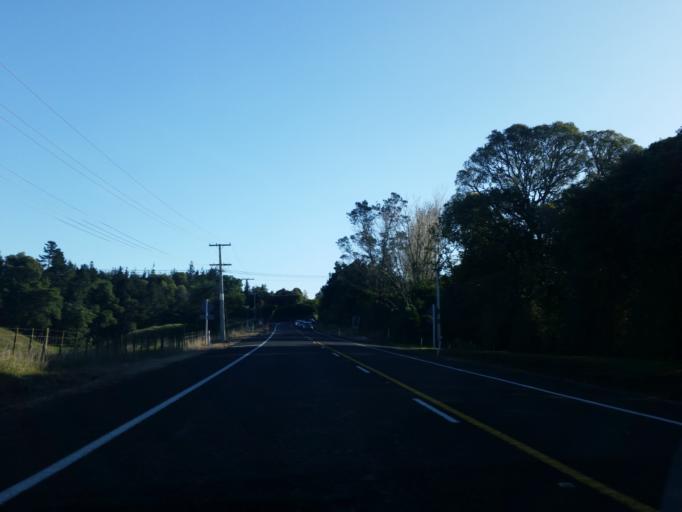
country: NZ
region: Bay of Plenty
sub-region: Western Bay of Plenty District
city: Katikati
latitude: -37.5313
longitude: 175.9149
